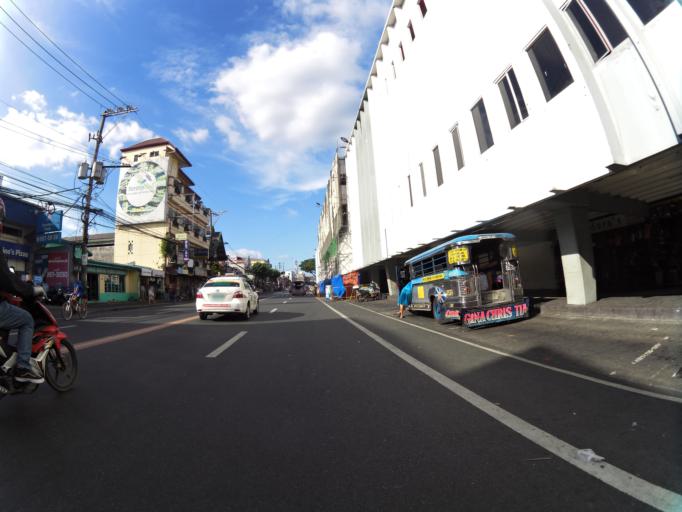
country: PH
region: Metro Manila
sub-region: Marikina
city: Calumpang
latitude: 14.6339
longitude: 121.0976
